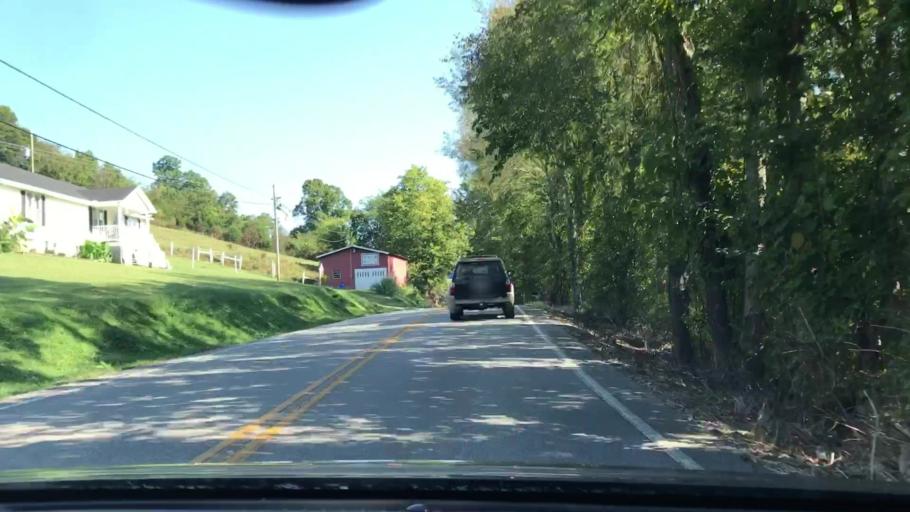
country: US
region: Tennessee
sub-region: Smith County
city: Carthage
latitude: 36.3486
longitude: -85.8965
